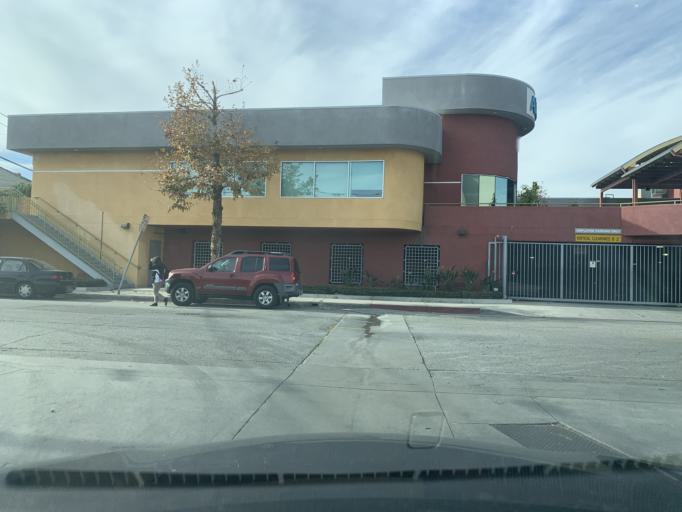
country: US
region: California
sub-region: Los Angeles County
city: El Monte
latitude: 34.0757
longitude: -118.0455
